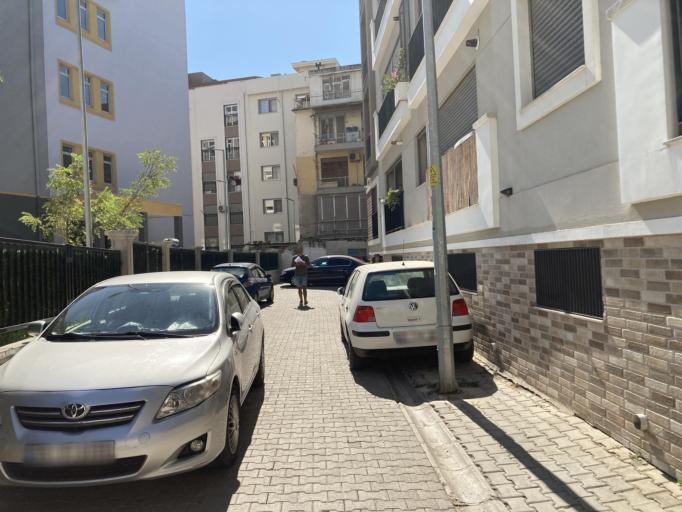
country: TR
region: Izmir
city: Karsiyaka
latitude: 38.4570
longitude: 27.1217
